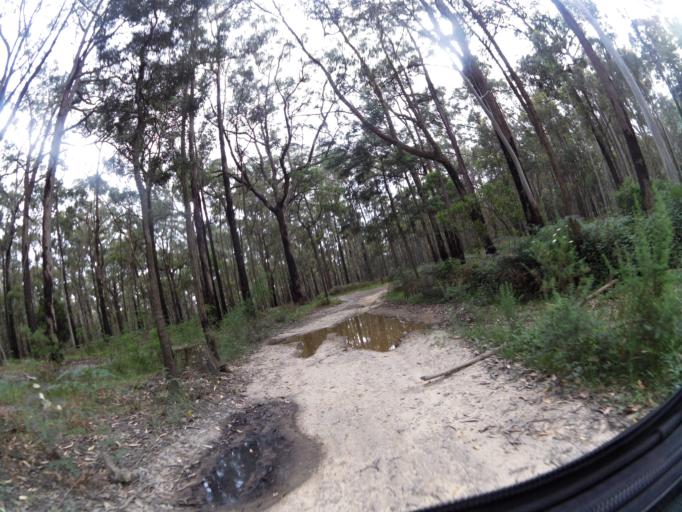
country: AU
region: Victoria
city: Brown Hill
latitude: -37.5042
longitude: 143.9076
